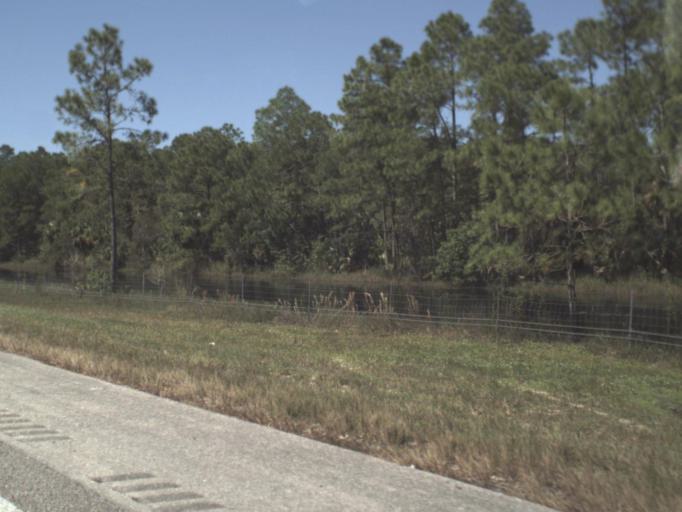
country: US
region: Florida
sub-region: Collier County
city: Golden Gate
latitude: 26.1544
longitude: -81.6166
